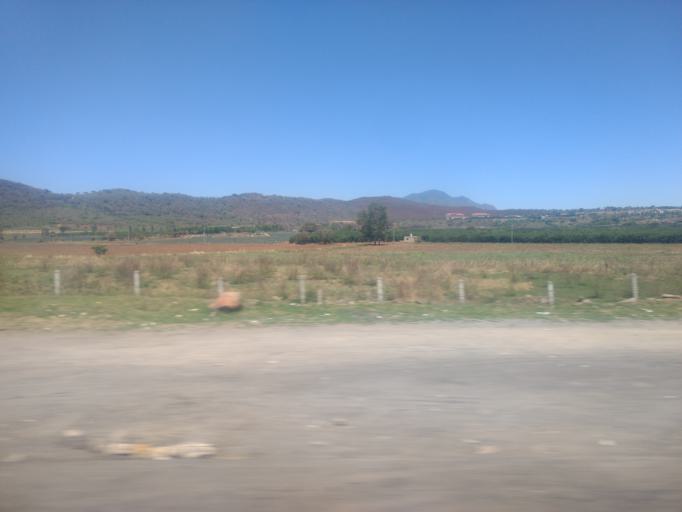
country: MX
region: Jalisco
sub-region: Acatlan de Juarez
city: Villa de los Ninos
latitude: 20.4144
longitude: -103.5575
